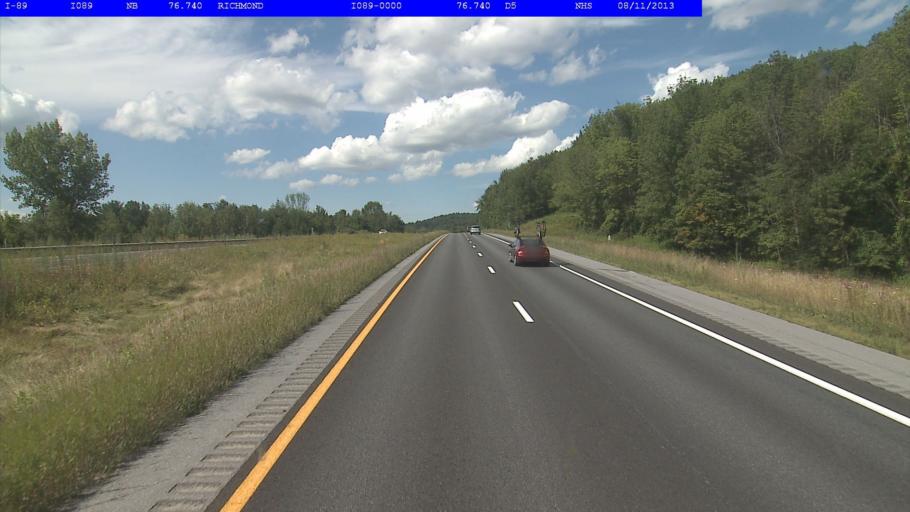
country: US
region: Vermont
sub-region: Chittenden County
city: Williston
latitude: 44.4069
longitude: -72.9897
